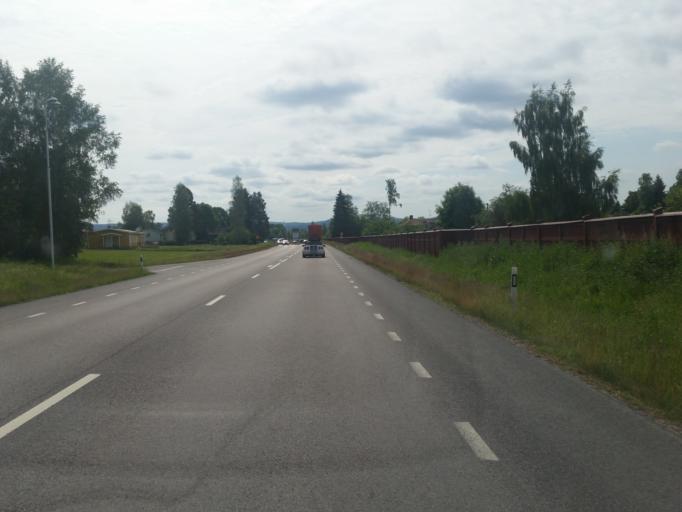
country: SE
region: Dalarna
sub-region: Gagnefs Kommun
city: Djuras
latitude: 60.5640
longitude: 15.1292
